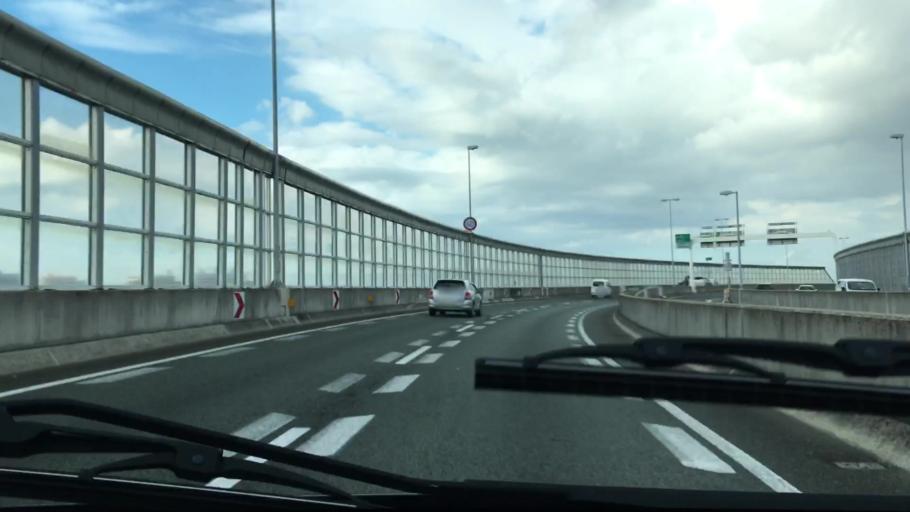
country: JP
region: Fukuoka
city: Fukuoka-shi
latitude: 33.5864
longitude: 130.3408
